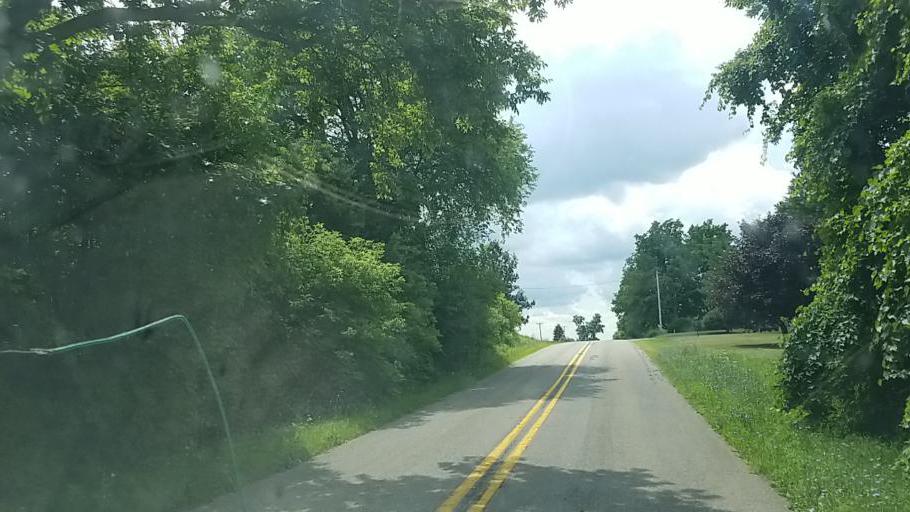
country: US
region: Michigan
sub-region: Kent County
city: Walker
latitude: 43.0699
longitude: -85.7485
